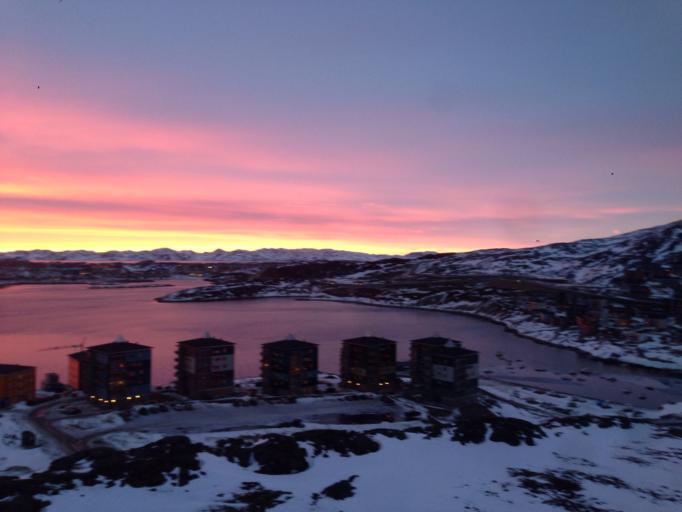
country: GL
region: Sermersooq
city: Nuuk
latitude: 64.1670
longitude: -51.6754
